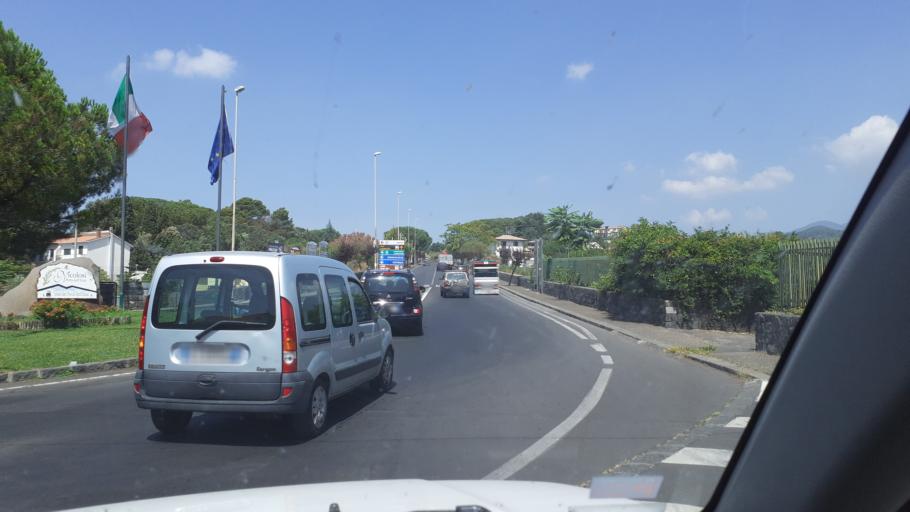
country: IT
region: Sicily
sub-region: Catania
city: Nicolosi
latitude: 37.6145
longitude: 15.0366
